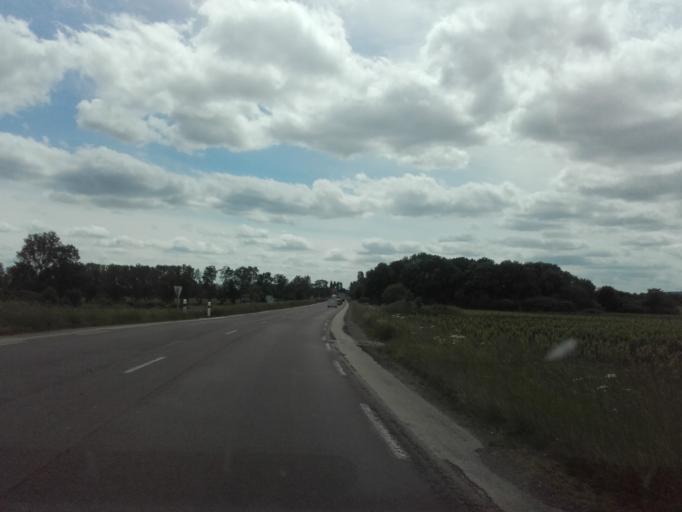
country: FR
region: Bourgogne
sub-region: Departement de la Cote-d'Or
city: Meursault
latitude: 46.9898
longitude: 4.7935
